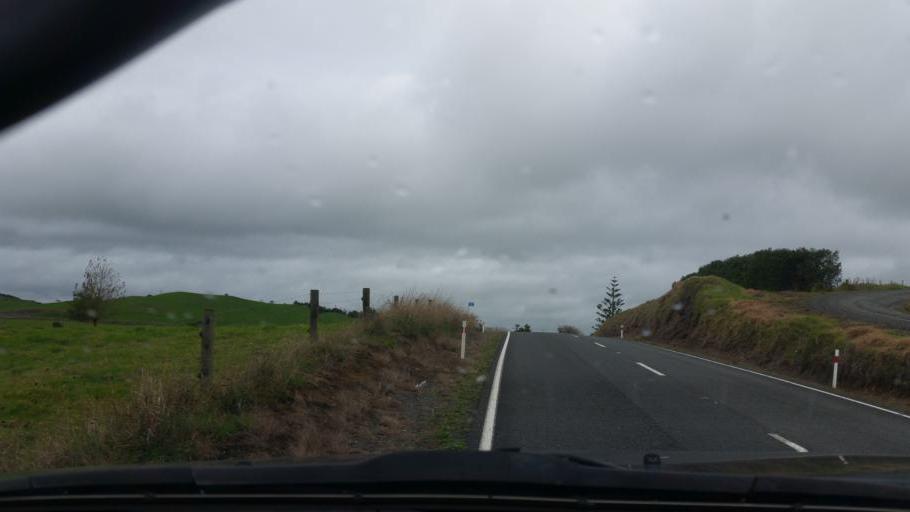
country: NZ
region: Northland
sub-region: Kaipara District
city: Dargaville
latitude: -36.0177
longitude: 173.9834
